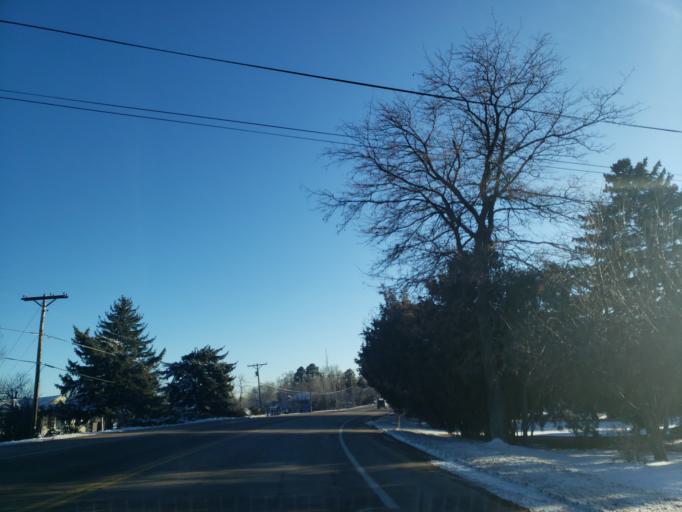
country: US
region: Colorado
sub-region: Larimer County
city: Fort Collins
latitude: 40.6275
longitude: -105.0709
